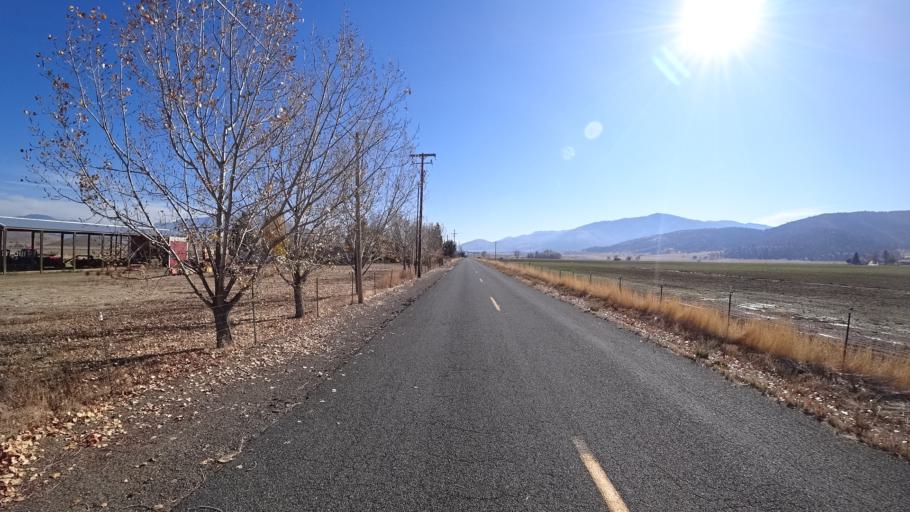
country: US
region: California
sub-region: Siskiyou County
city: Montague
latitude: 41.5436
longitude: -122.5392
